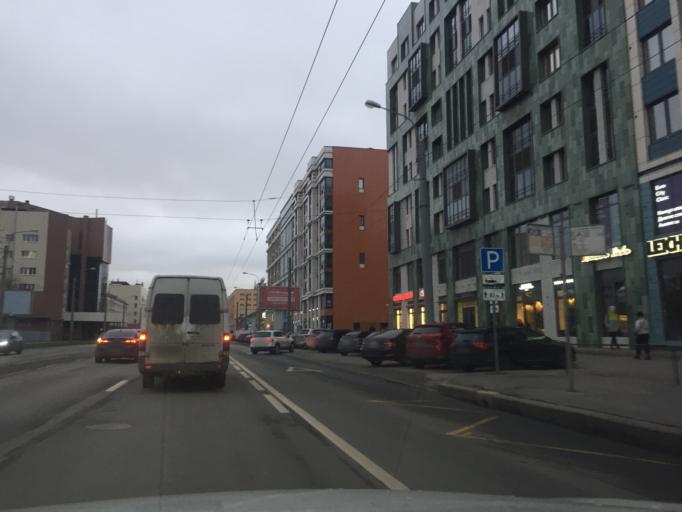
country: RU
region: St.-Petersburg
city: Petrogradka
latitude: 59.9747
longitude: 30.3168
